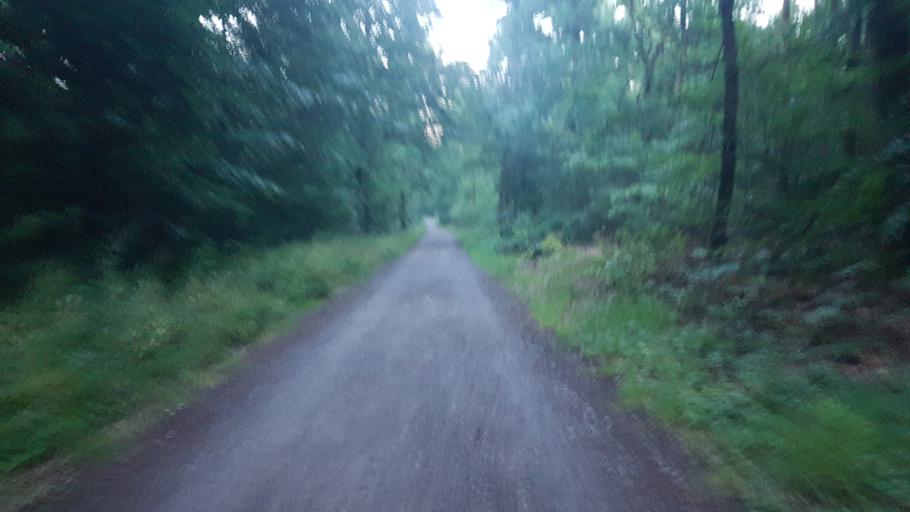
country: DE
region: Baden-Wuerttemberg
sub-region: Regierungsbezirk Stuttgart
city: Brackenheim
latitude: 49.1041
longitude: 9.0322
